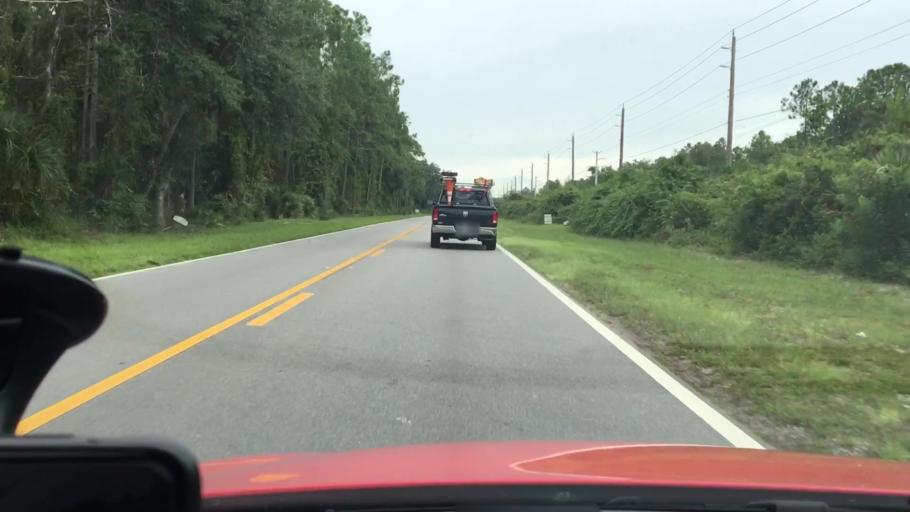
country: US
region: Florida
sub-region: Flagler County
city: Palm Coast
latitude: 29.5150
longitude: -81.1964
